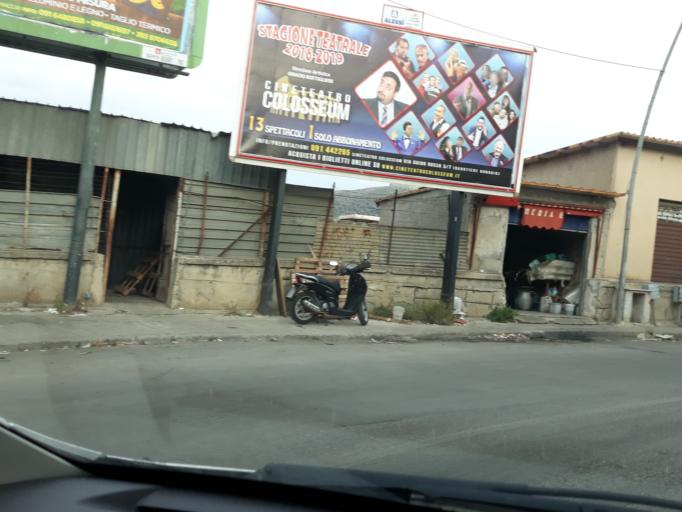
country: IT
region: Sicily
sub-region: Palermo
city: Villa Ciambra
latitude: 38.0861
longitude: 13.3522
